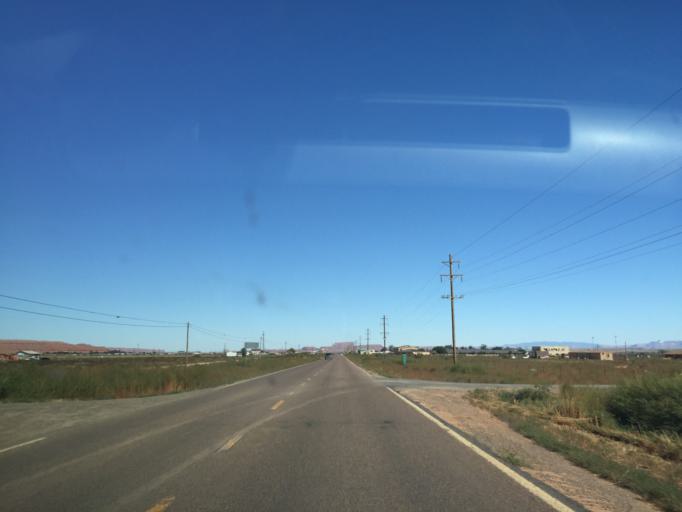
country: US
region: Arizona
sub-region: Apache County
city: Many Farms
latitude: 36.3427
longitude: -109.6222
